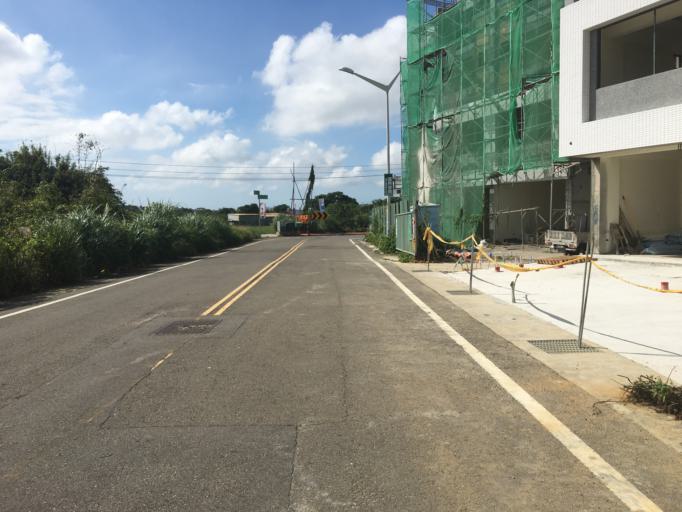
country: TW
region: Taiwan
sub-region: Hsinchu
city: Zhubei
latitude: 24.8905
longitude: 121.0499
